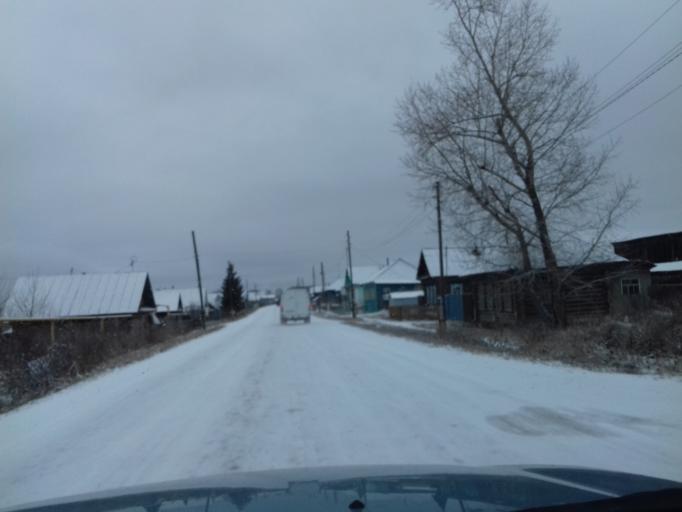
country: RU
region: Sverdlovsk
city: Sarana
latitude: 56.3027
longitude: 57.9869
